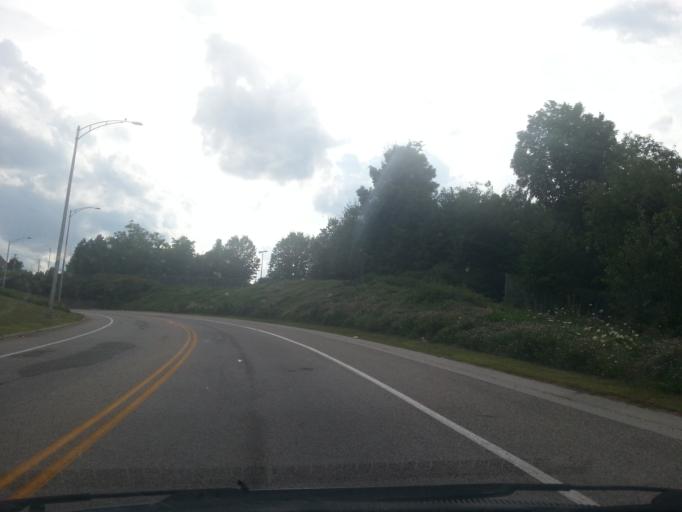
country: CA
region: Quebec
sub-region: Outaouais
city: Gatineau
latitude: 45.4929
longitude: -75.7355
